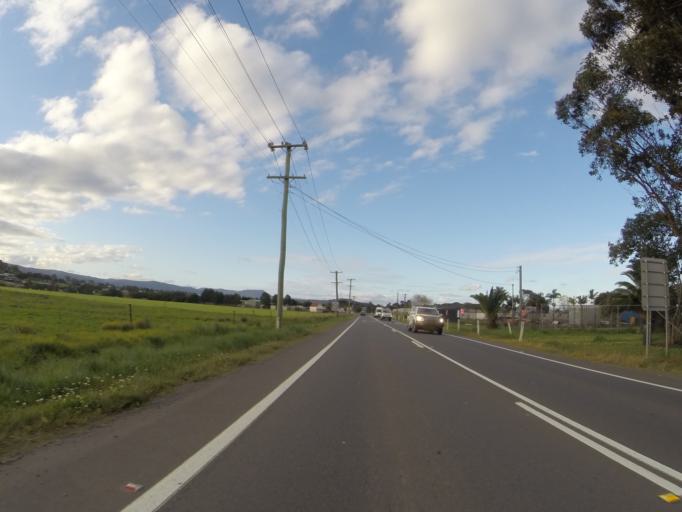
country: AU
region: New South Wales
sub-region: Shellharbour
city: Albion Park Rail
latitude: -34.5515
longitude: 150.7831
